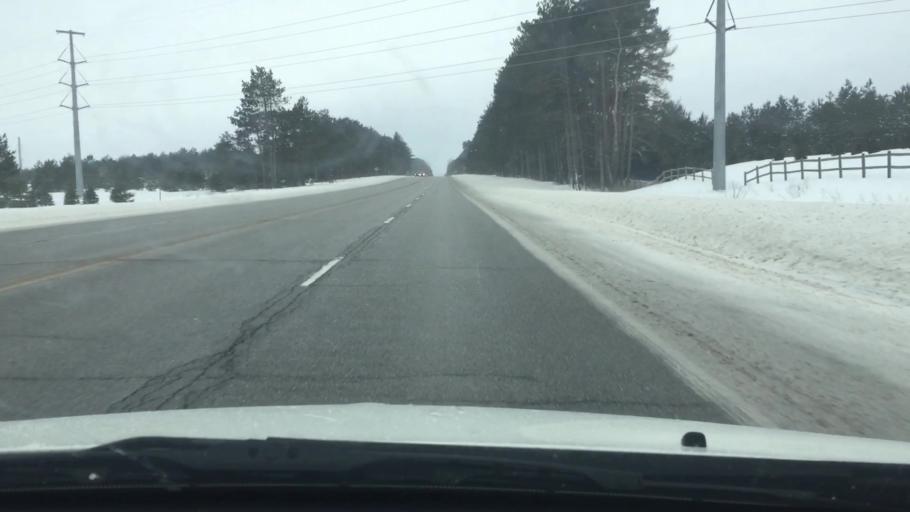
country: US
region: Michigan
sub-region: Otsego County
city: Gaylord
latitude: 45.0621
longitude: -84.8292
